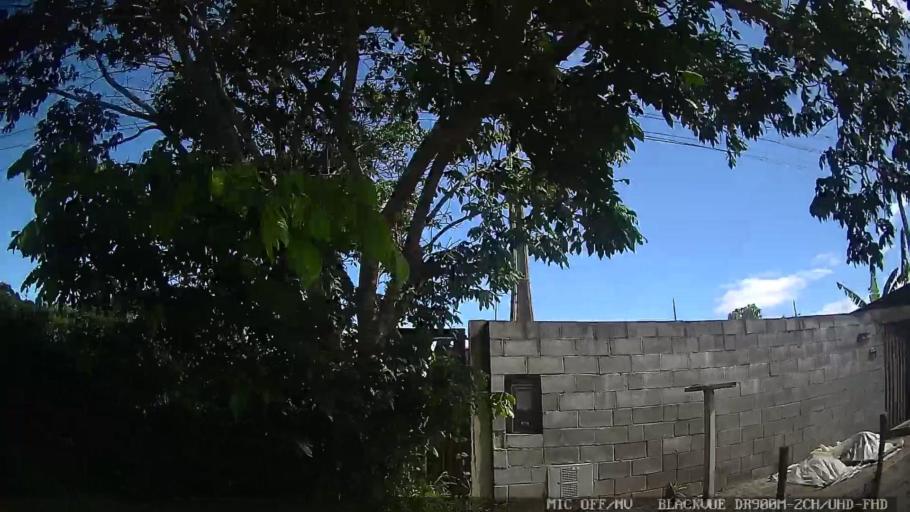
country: BR
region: Sao Paulo
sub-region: Itanhaem
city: Itanhaem
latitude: -24.2230
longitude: -46.8708
